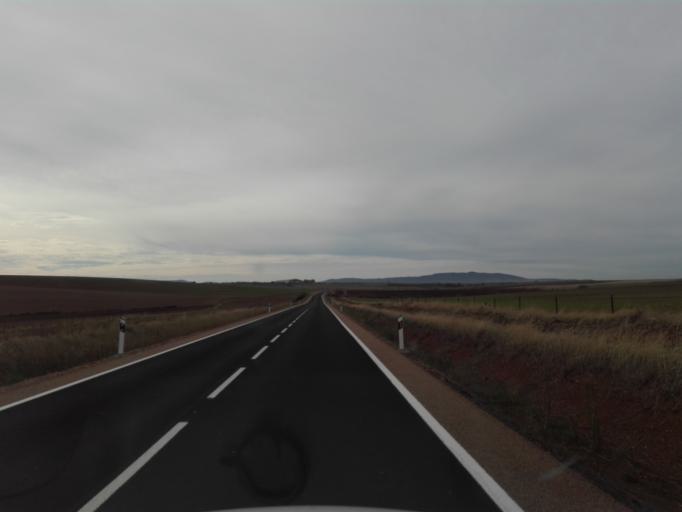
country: ES
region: Extremadura
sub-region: Provincia de Badajoz
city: Valencia de las Torres
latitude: 38.3396
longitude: -5.9641
